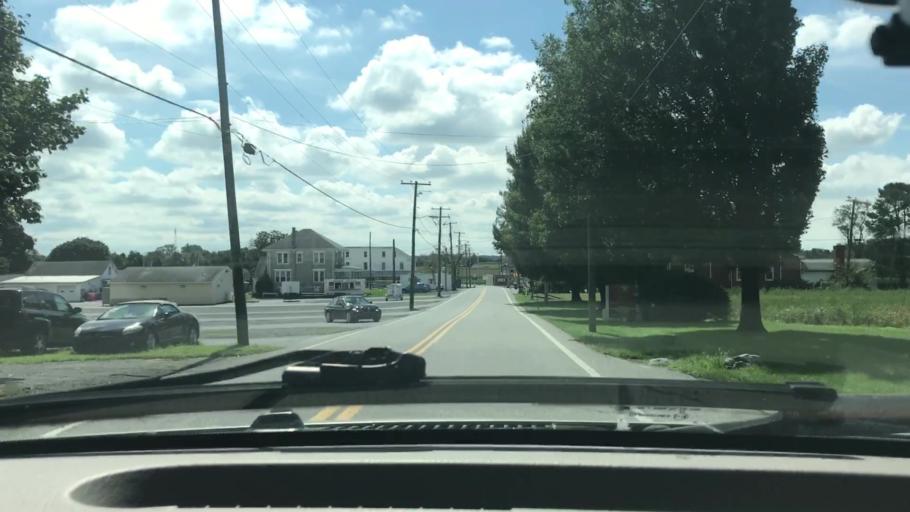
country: US
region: Pennsylvania
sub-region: Lancaster County
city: East Petersburg
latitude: 40.1200
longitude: -76.3794
